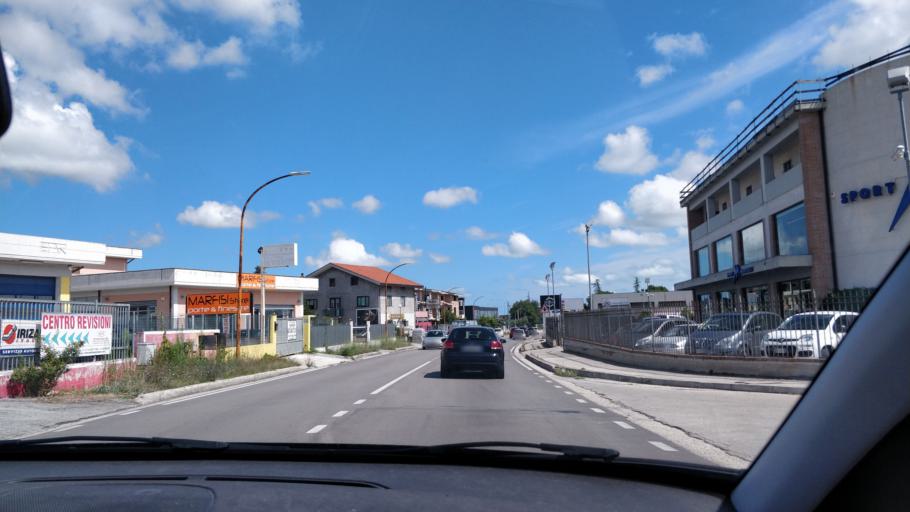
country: IT
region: Abruzzo
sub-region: Provincia di Chieti
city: Lanciano
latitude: 42.2387
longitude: 14.4095
